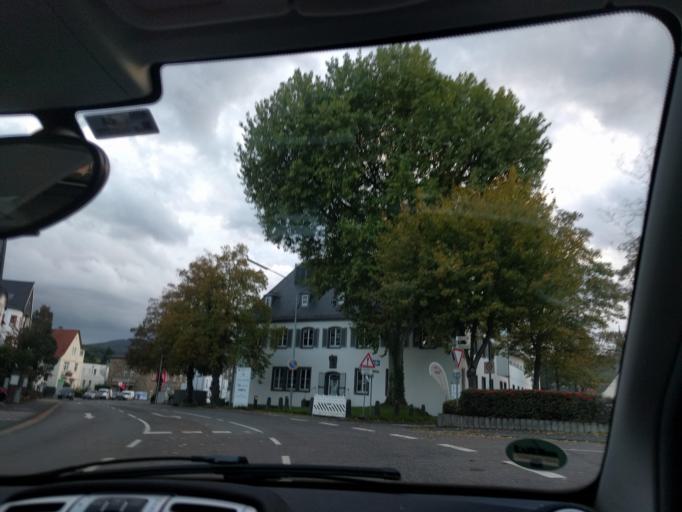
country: DE
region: Rheinland-Pfalz
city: Bad Neuenahr-Ahrweiler
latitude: 50.5460
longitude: 7.1024
